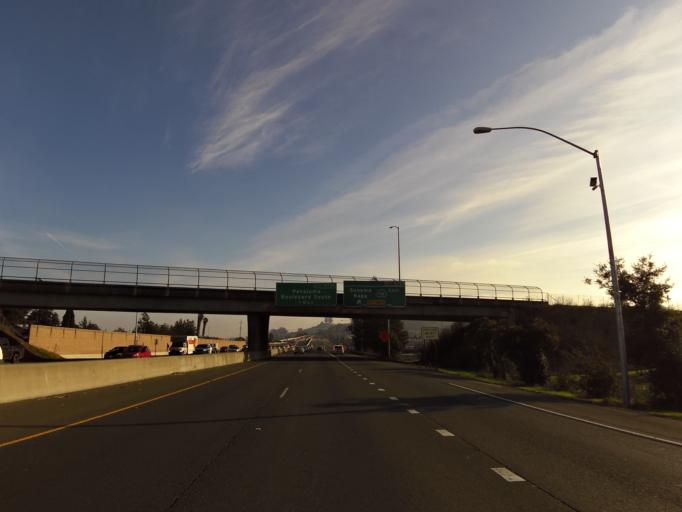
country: US
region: California
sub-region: Sonoma County
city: Petaluma
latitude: 38.2382
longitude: -122.6205
